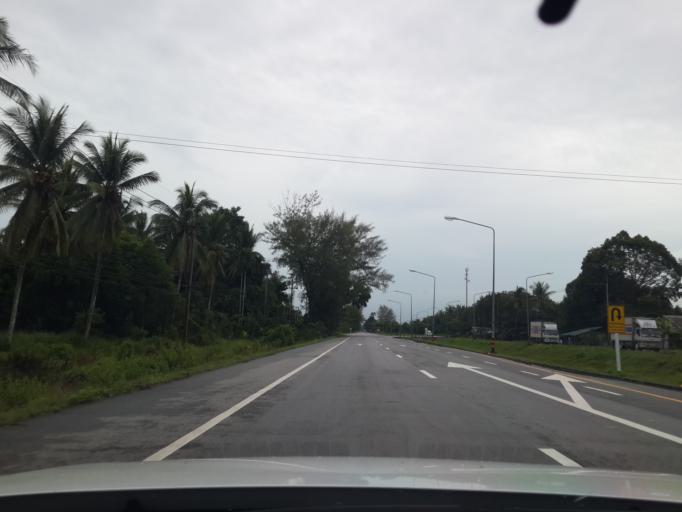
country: TH
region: Songkhla
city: Thepha
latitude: 6.8258
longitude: 101.0505
